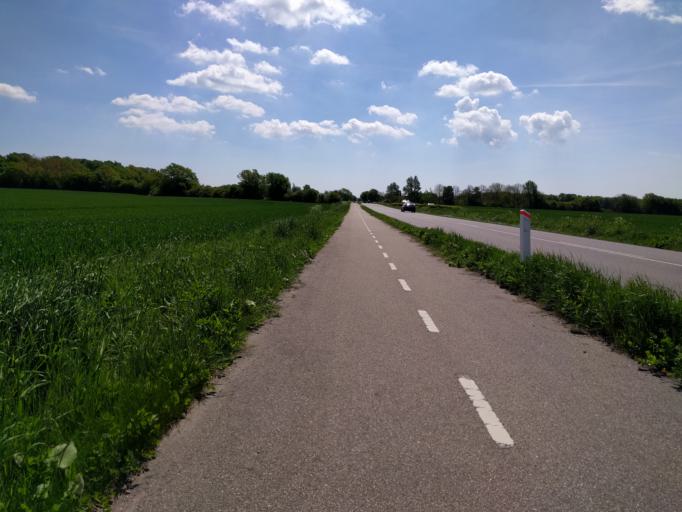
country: DK
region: Zealand
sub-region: Guldborgsund Kommune
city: Nykobing Falster
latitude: 54.7535
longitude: 11.9319
